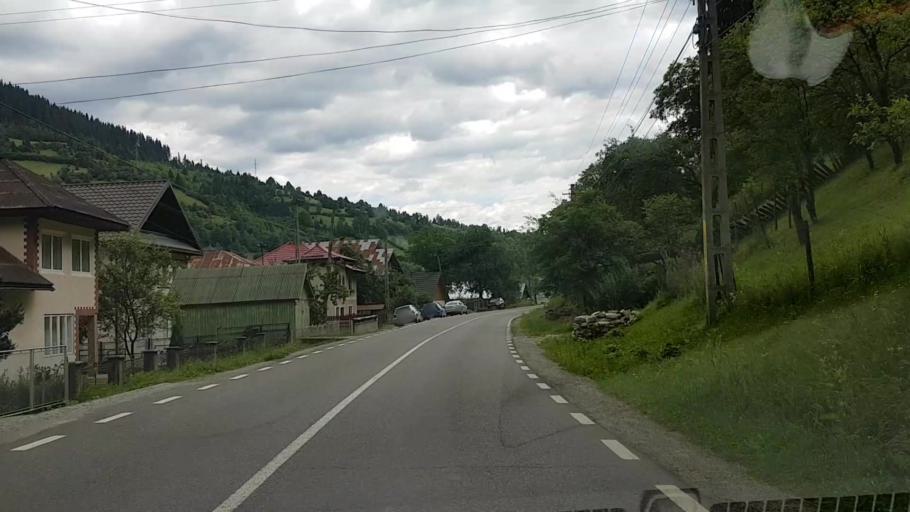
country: RO
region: Neamt
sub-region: Comuna Borca
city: Borca
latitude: 47.2156
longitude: 25.7546
